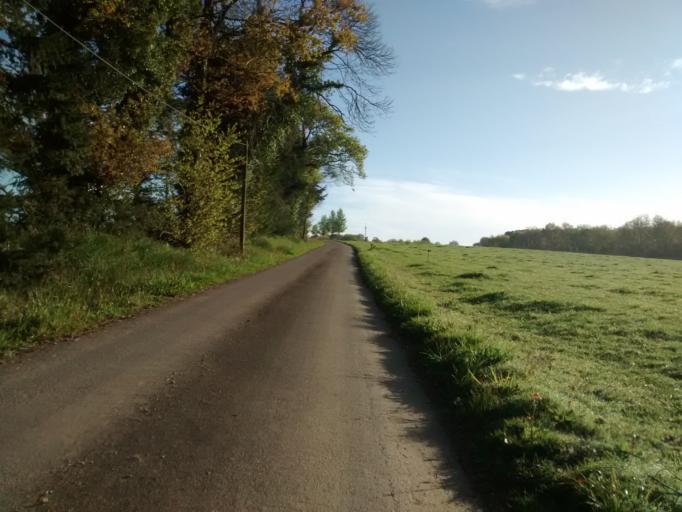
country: FR
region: Brittany
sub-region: Departement du Morbihan
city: Malestroit
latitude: 47.7983
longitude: -2.4005
